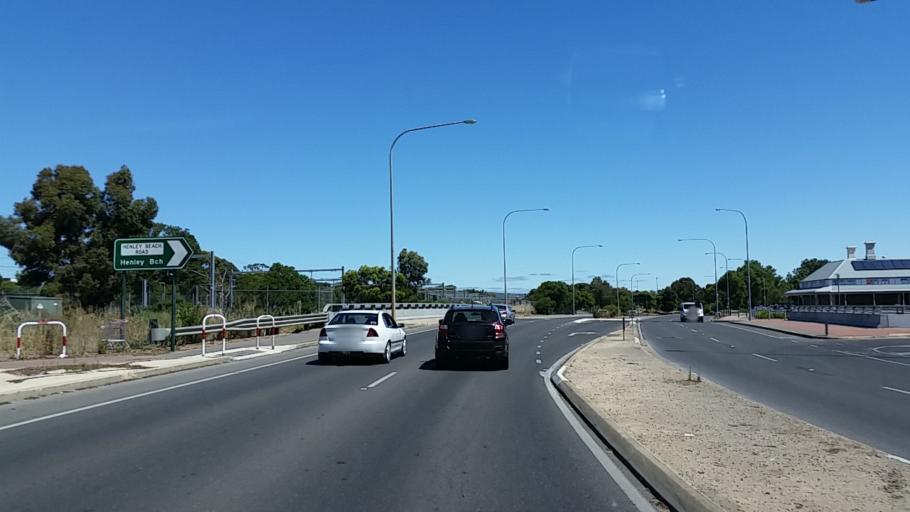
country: AU
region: South Australia
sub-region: City of West Torrens
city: Thebarton
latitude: -34.9228
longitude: 138.5794
